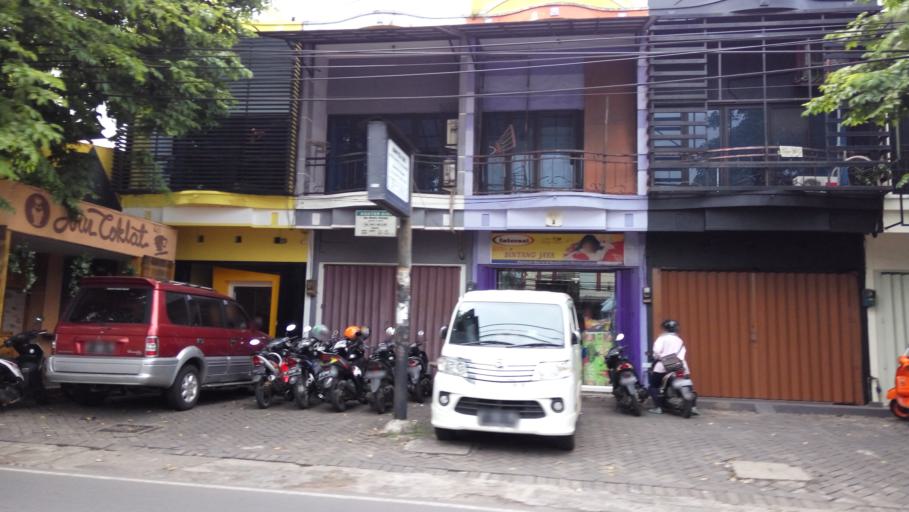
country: ID
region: East Java
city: Malang
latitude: -7.9485
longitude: 112.6088
